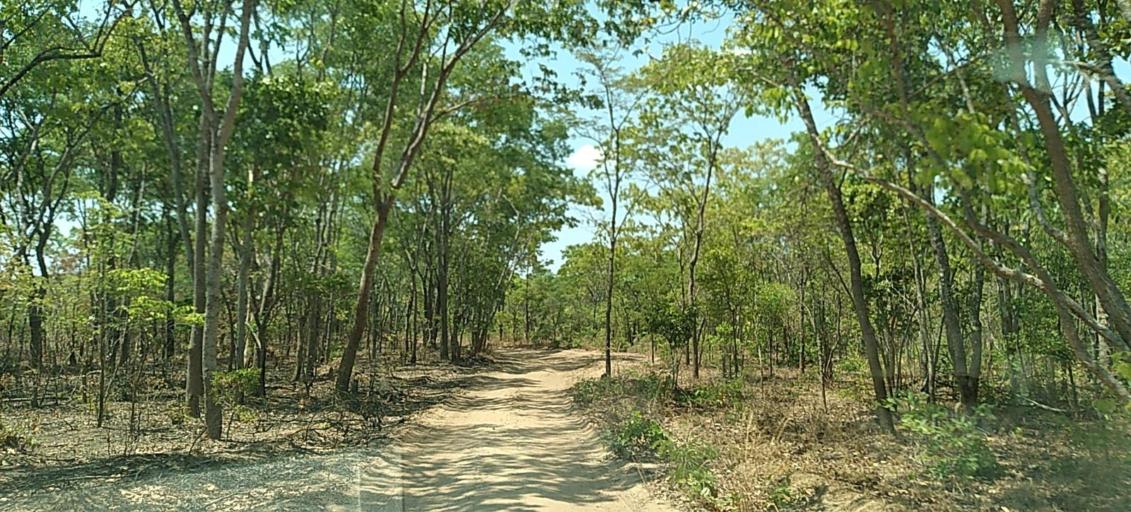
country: ZM
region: Copperbelt
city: Mpongwe
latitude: -13.6442
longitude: 28.4846
